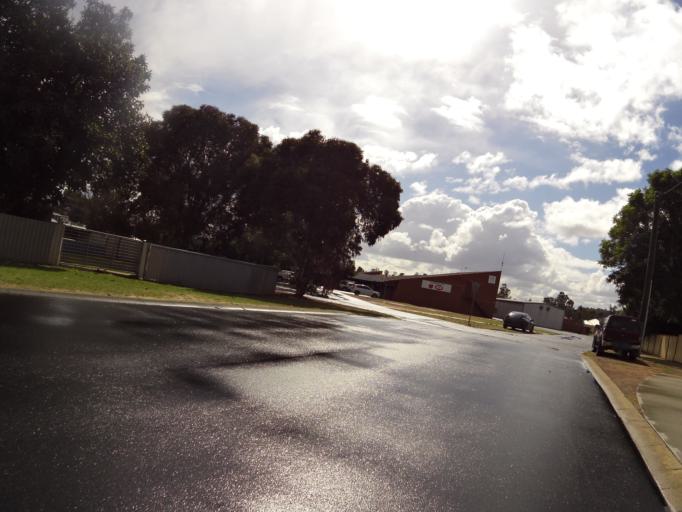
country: AU
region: Western Australia
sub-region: Donnybrook-Balingup
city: Donnybrook
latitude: -33.5709
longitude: 115.8243
